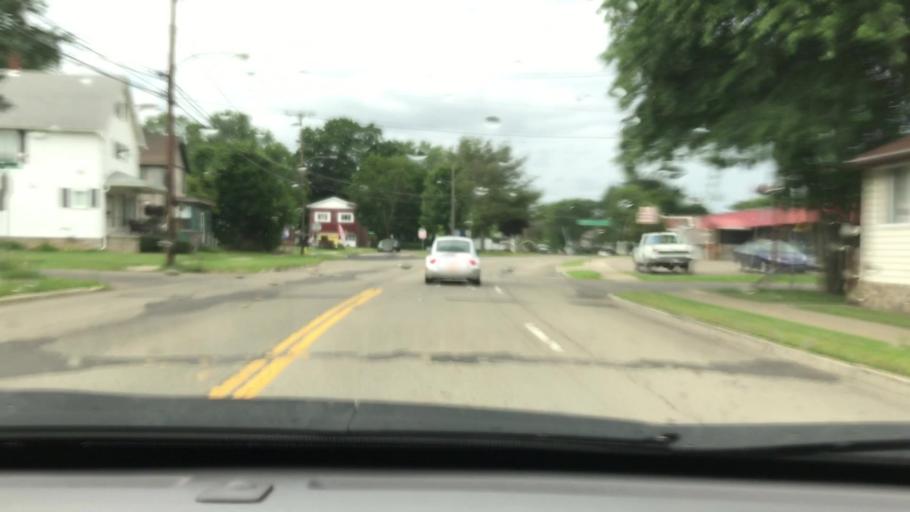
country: US
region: New York
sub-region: Cattaraugus County
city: Salamanca
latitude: 42.1654
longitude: -78.6950
